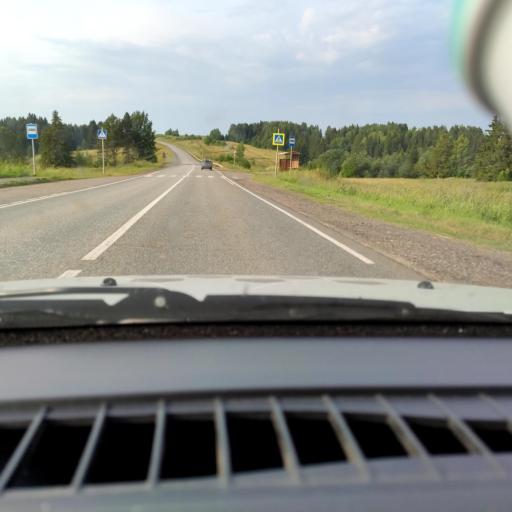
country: RU
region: Udmurtiya
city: Balezino
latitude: 57.8117
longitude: 52.9722
